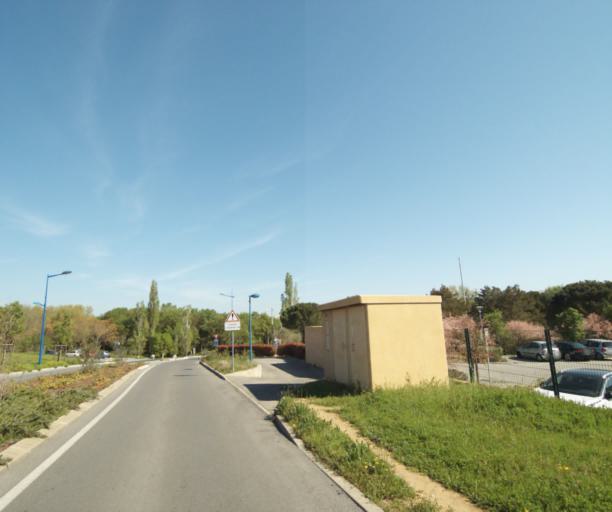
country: FR
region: Languedoc-Roussillon
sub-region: Departement de l'Herault
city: Le Cres
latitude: 43.6552
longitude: 3.9353
